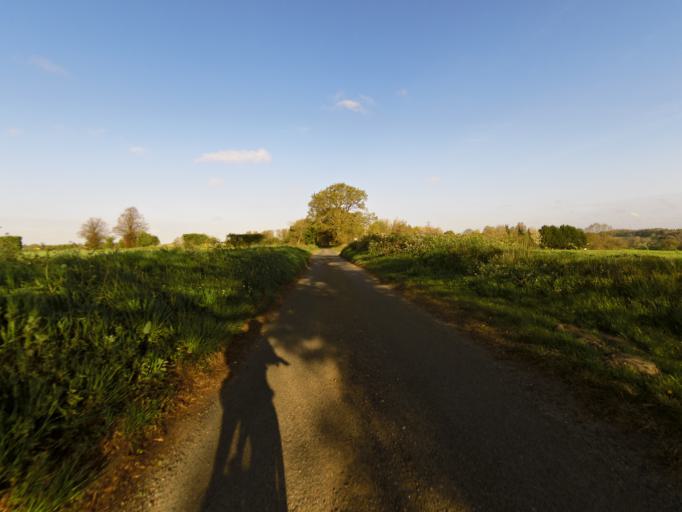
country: GB
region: England
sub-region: Suffolk
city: Bramford
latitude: 52.0453
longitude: 1.0688
